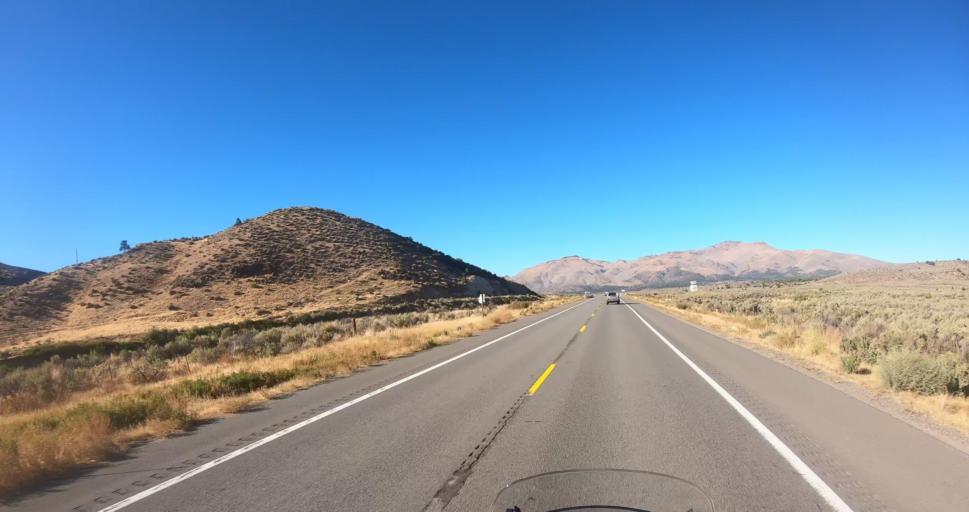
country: US
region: Nevada
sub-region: Washoe County
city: Cold Springs
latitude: 39.9271
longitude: -120.0185
